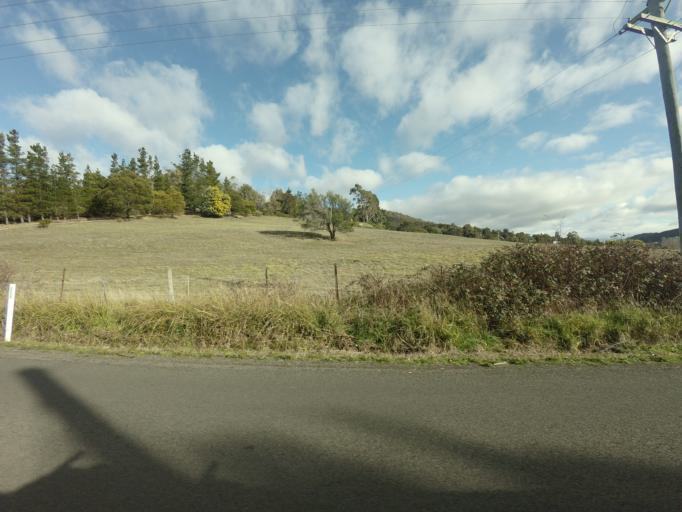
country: AU
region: Tasmania
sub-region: Derwent Valley
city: New Norfolk
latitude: -42.7846
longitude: 147.1173
